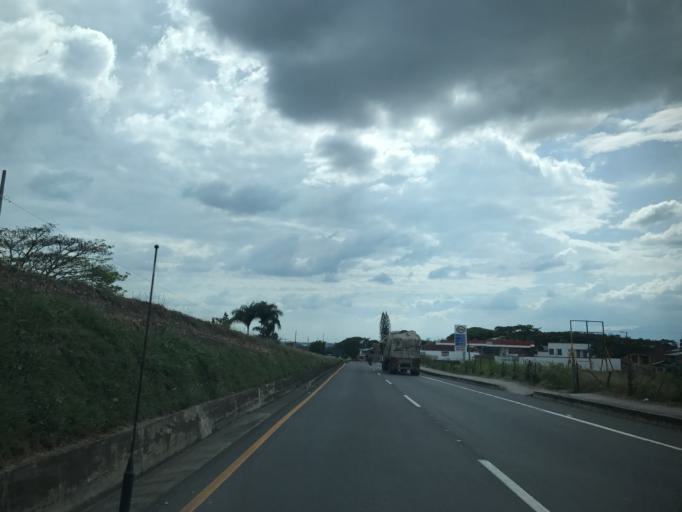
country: CO
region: Valle del Cauca
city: Cartago
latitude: 4.7654
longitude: -75.8954
